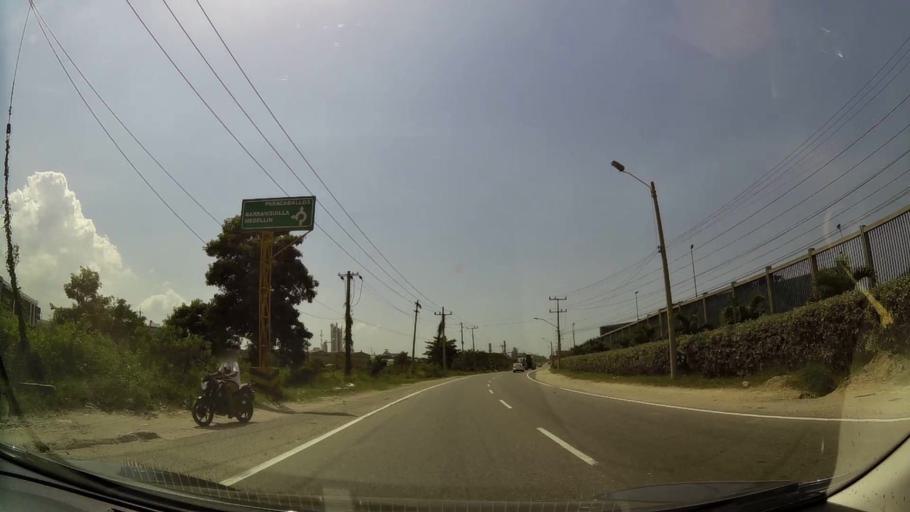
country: CO
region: Bolivar
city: Cartagena
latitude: 10.3450
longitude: -75.4952
